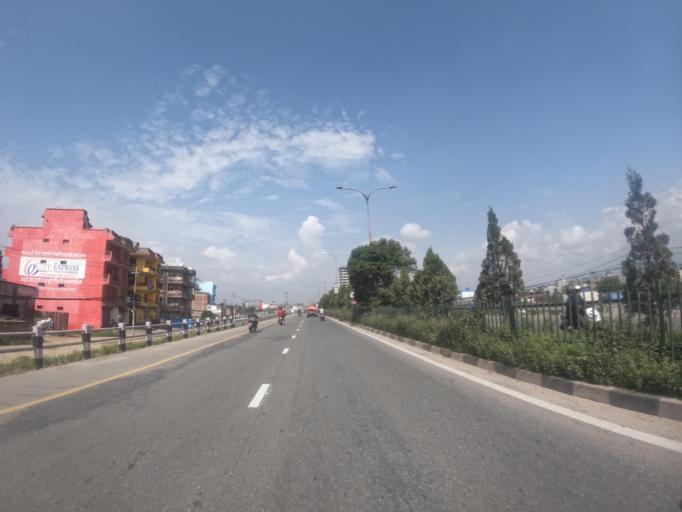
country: NP
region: Central Region
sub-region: Bagmati Zone
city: Bhaktapur
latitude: 27.6737
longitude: 85.4013
